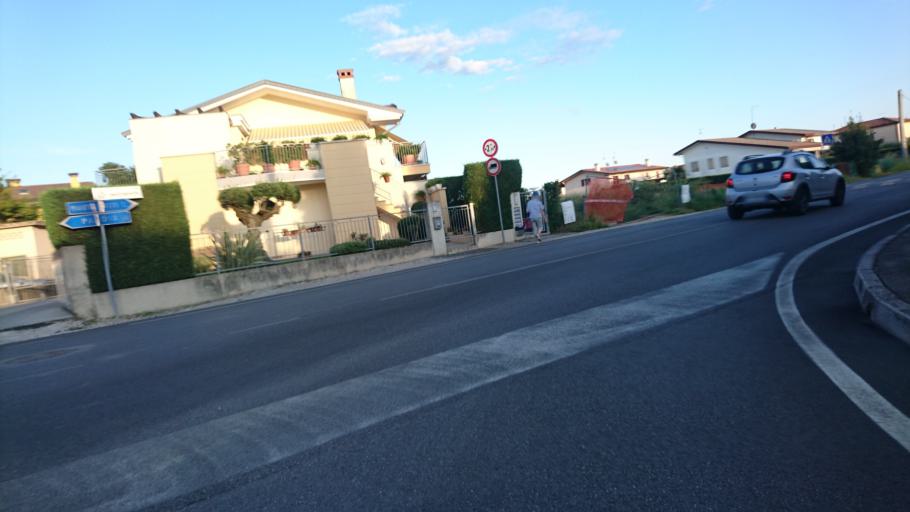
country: IT
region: Veneto
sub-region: Provincia di Padova
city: Montegrotto Terme
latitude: 45.3409
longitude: 11.7762
